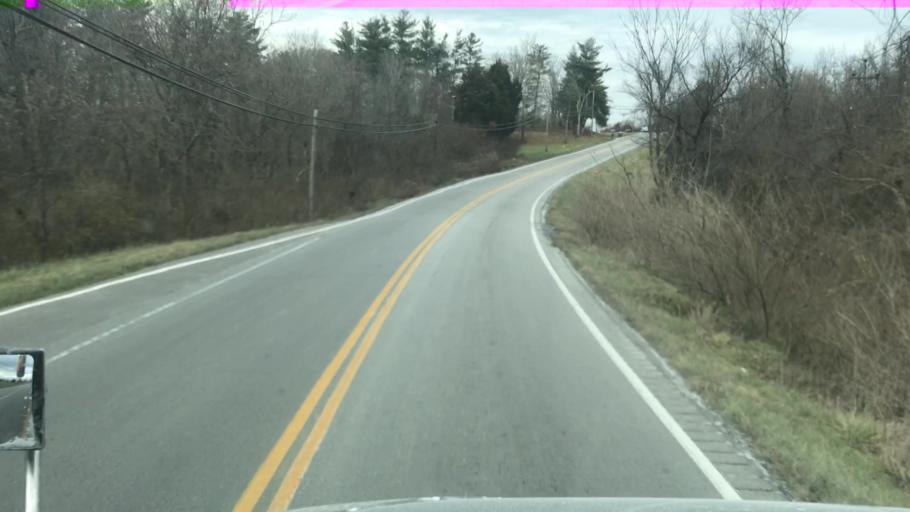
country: US
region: Kentucky
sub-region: Boone County
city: Walton
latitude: 38.9140
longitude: -84.6216
